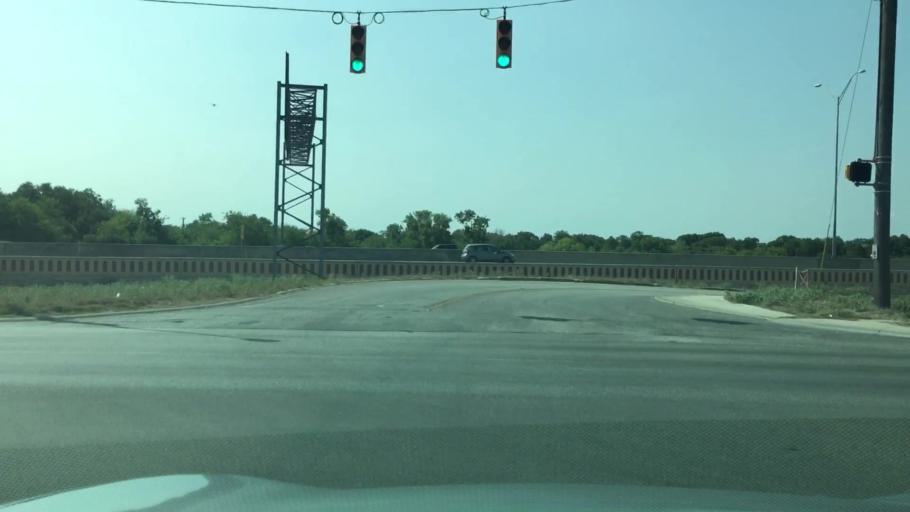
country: US
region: Texas
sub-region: Comal County
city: New Braunfels
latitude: 29.6946
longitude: -98.1050
